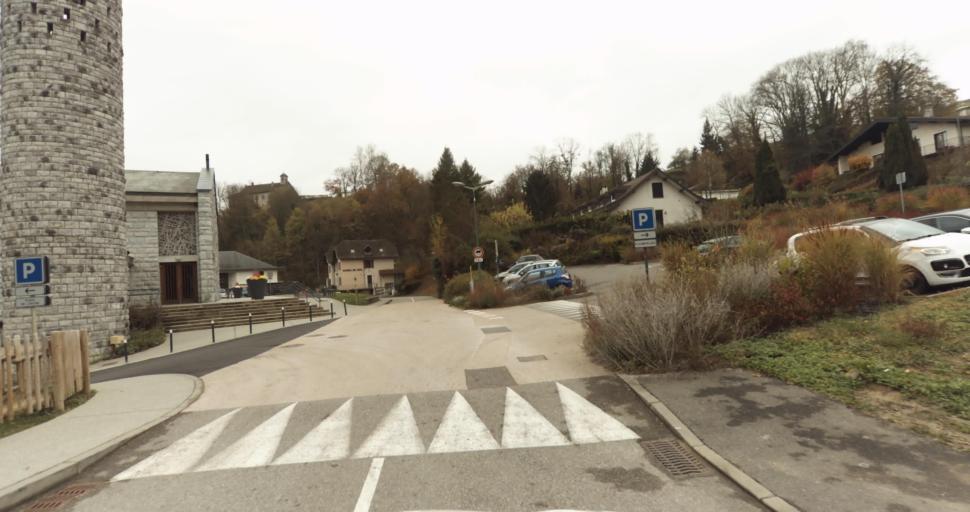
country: FR
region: Rhone-Alpes
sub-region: Departement de la Haute-Savoie
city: Alby-sur-Cheran
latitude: 45.8190
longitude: 6.0196
